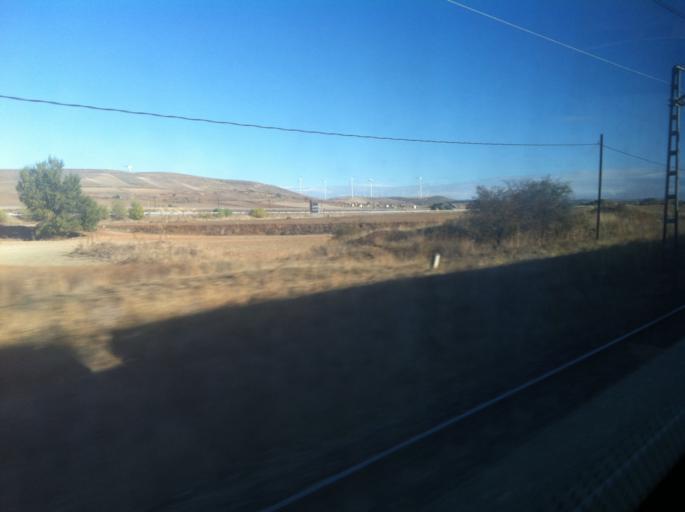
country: ES
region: Castille and Leon
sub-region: Provincia de Burgos
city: Villazopeque
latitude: 42.1888
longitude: -4.0334
